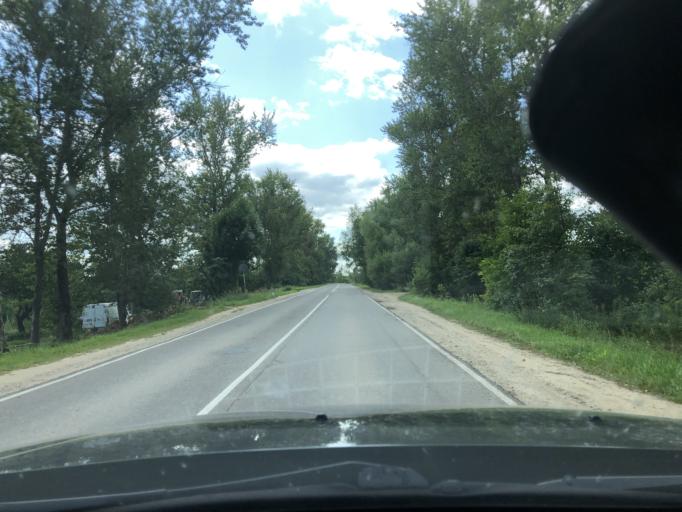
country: RU
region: Tula
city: Revyakino
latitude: 54.3568
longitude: 37.6355
